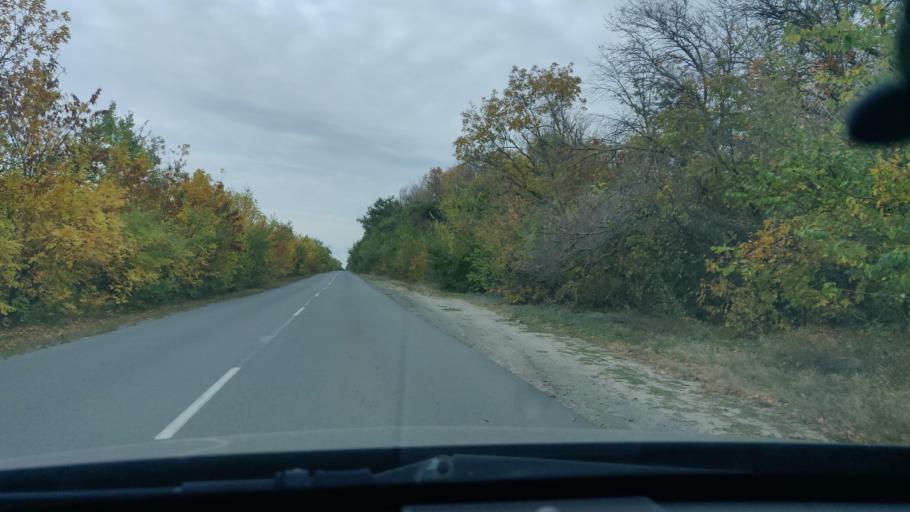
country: RU
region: Rostov
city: Ust'-Donetskiy
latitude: 47.6521
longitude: 40.8921
